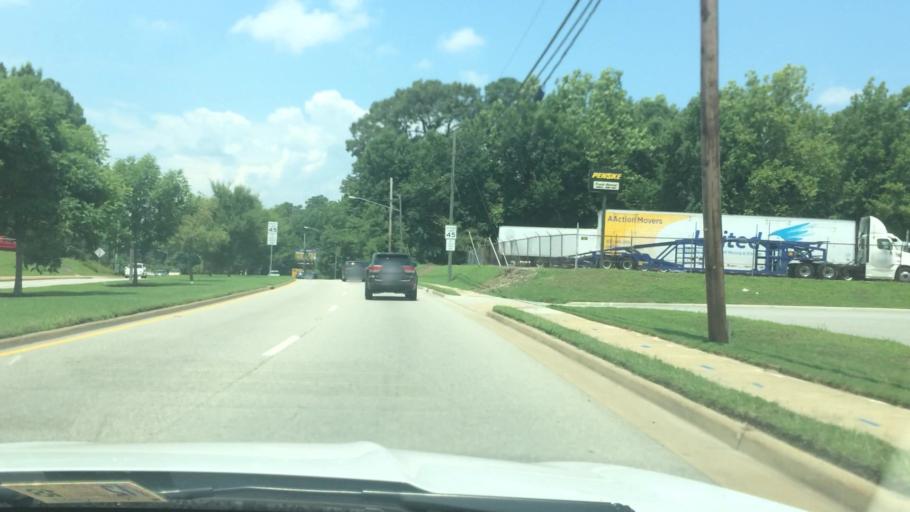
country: US
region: Virginia
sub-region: York County
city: Yorktown
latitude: 37.1646
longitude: -76.5573
